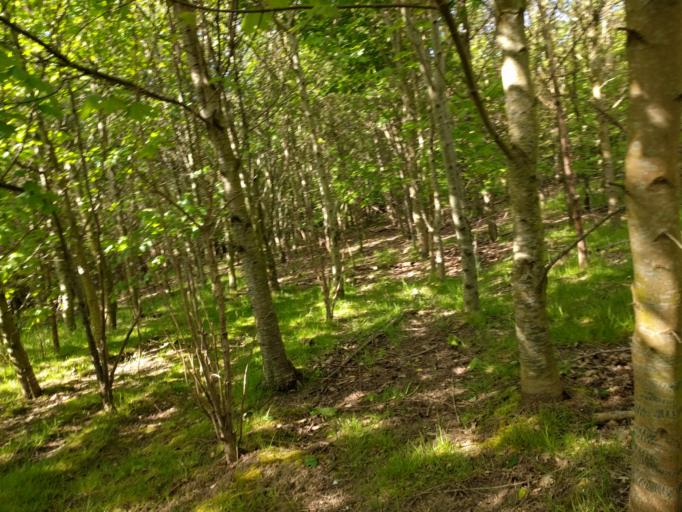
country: DK
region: Zealand
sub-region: Guldborgsund Kommune
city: Stubbekobing
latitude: 54.9246
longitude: 12.0085
